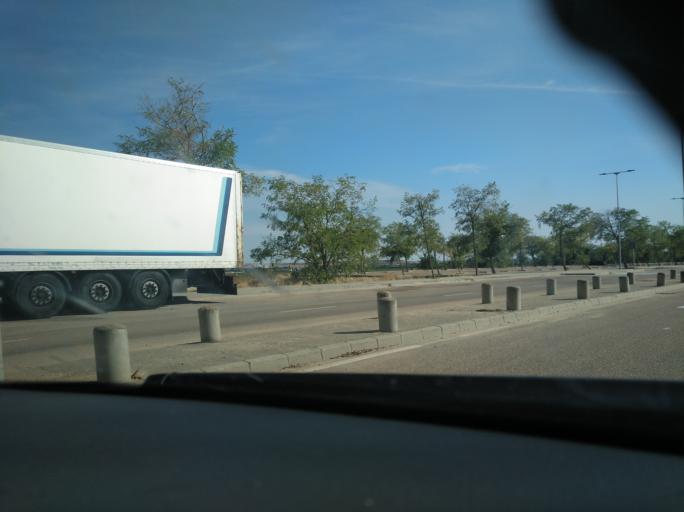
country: ES
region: Extremadura
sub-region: Provincia de Badajoz
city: Badajoz
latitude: 38.8816
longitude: -7.0252
